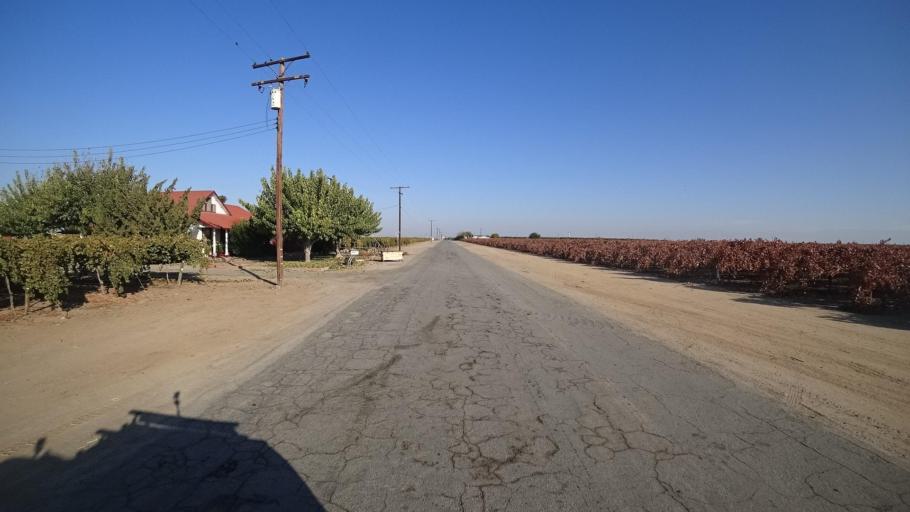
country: US
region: California
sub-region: Tulare County
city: Richgrove
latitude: 35.7697
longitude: -119.1518
